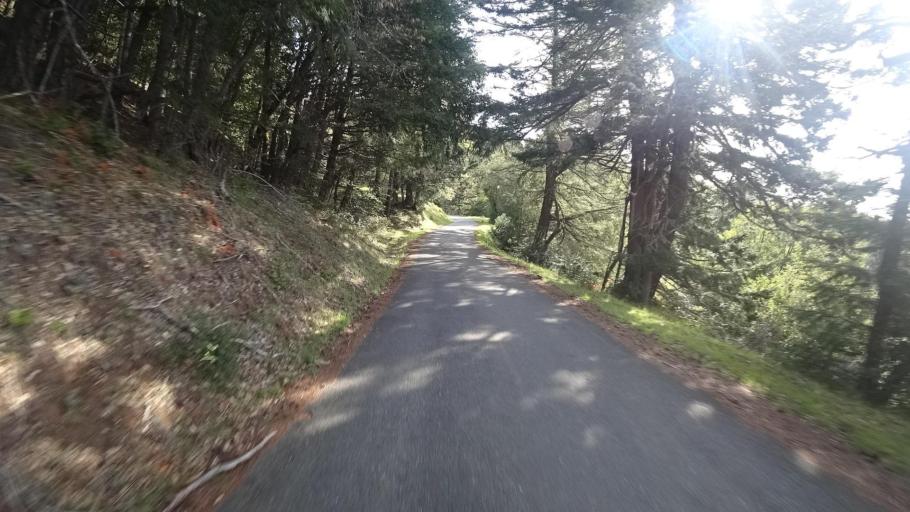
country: US
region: California
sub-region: Humboldt County
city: Hydesville
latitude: 40.6429
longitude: -123.9088
